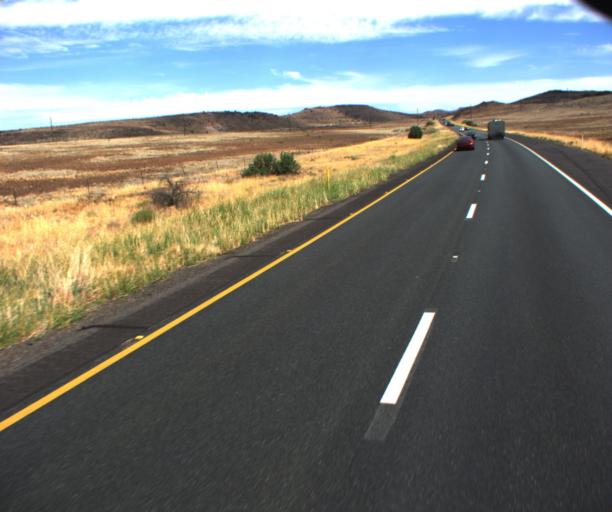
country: US
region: Arizona
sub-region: Yavapai County
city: Cordes Lakes
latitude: 34.4368
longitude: -112.0314
